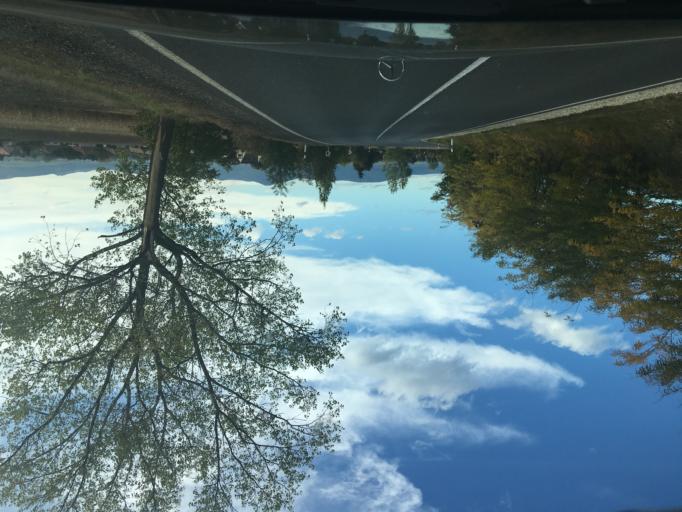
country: HU
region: Borsod-Abauj-Zemplen
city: Encs
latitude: 48.3581
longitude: 21.1356
